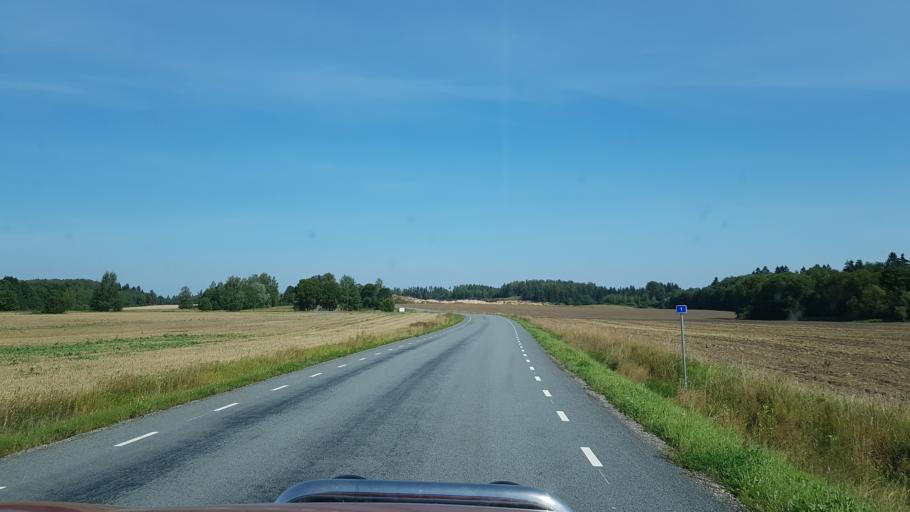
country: EE
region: Viljandimaa
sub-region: Vohma linn
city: Vohma
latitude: 58.5047
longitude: 25.6053
